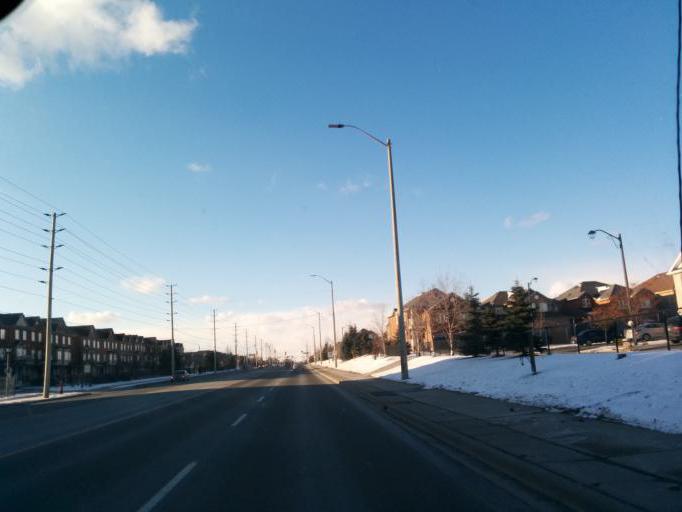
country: CA
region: Ontario
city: Brampton
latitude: 43.6331
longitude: -79.7119
